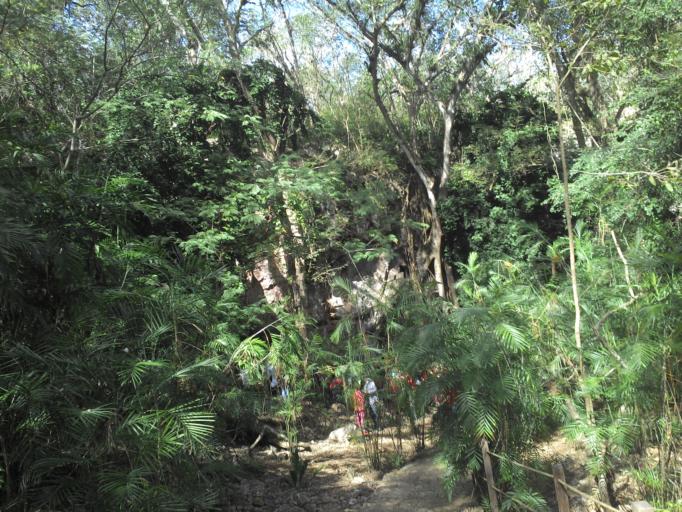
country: MX
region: Yucatan
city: Oxkutzkab
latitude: 20.2539
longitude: -89.4559
